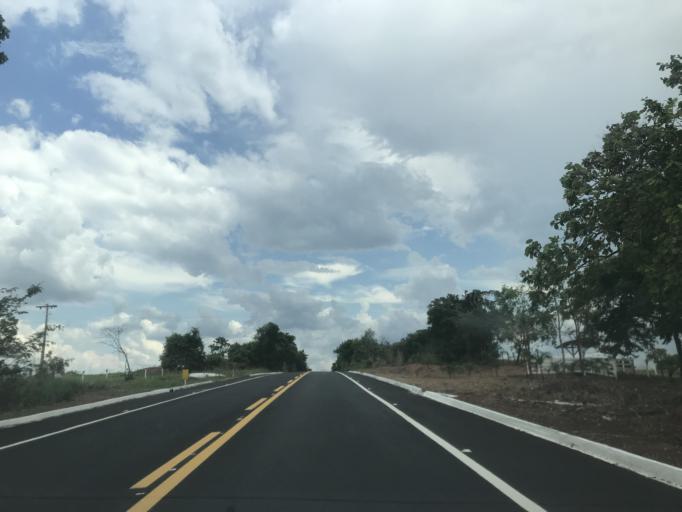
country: BR
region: Goias
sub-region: Caldas Novas
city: Caldas Novas
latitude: -17.7256
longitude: -48.7754
